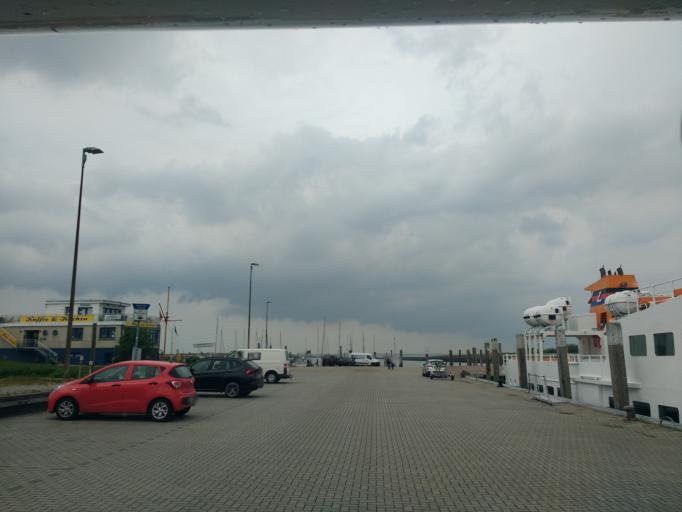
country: DE
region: Lower Saxony
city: Holtgast
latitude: 53.6767
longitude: 7.5725
